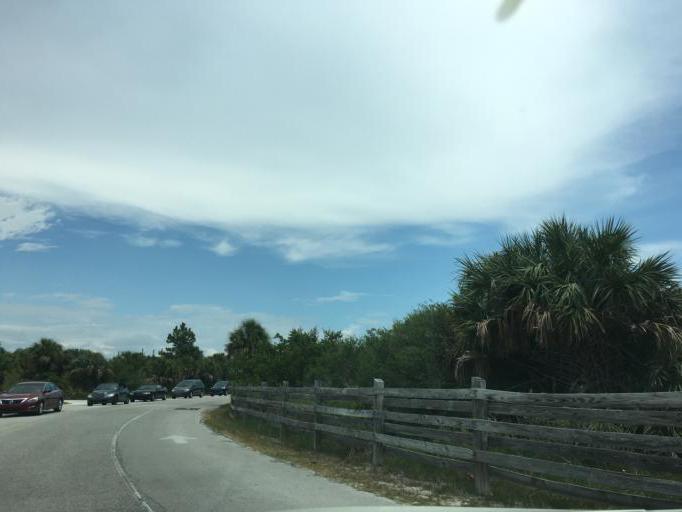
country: US
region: Florida
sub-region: Pinellas County
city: Palm Harbor
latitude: 28.0607
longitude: -82.8186
